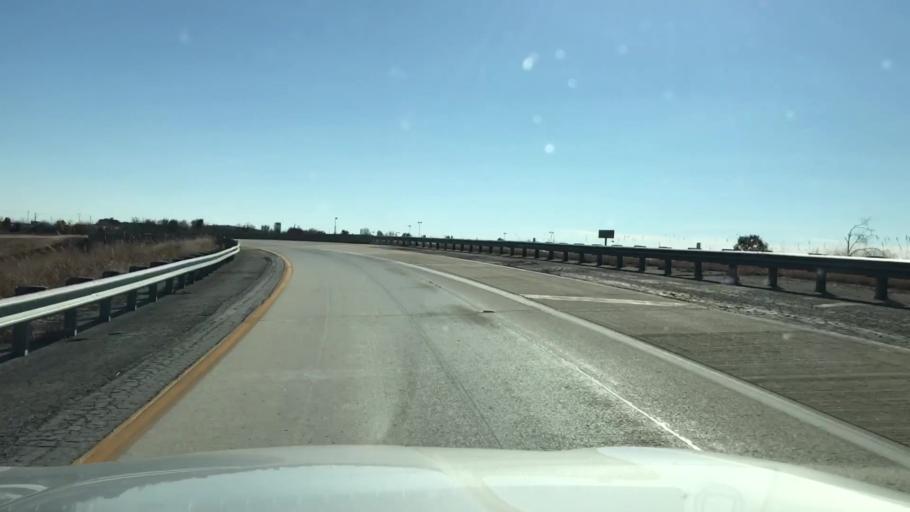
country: US
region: Missouri
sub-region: Jasper County
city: Duenweg
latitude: 37.0614
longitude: -94.4303
